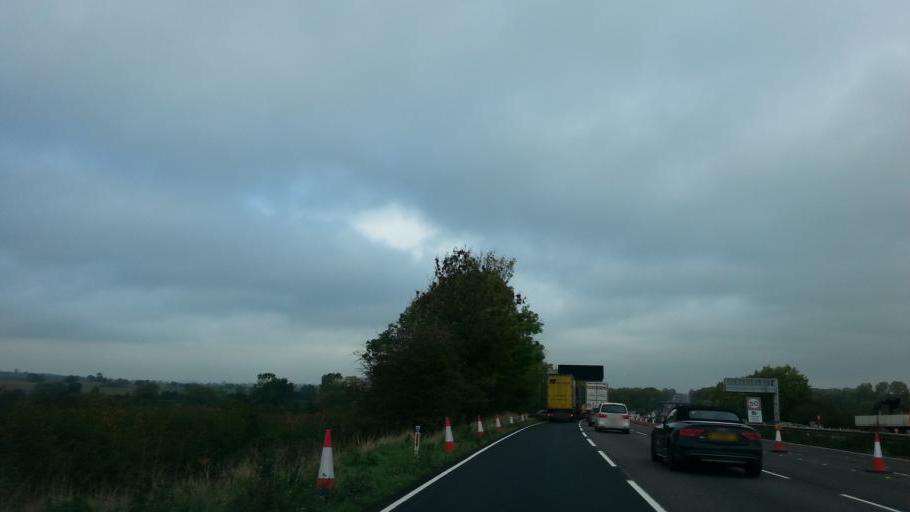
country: GB
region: England
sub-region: Staffordshire
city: Stafford
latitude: 52.8442
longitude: -2.1578
